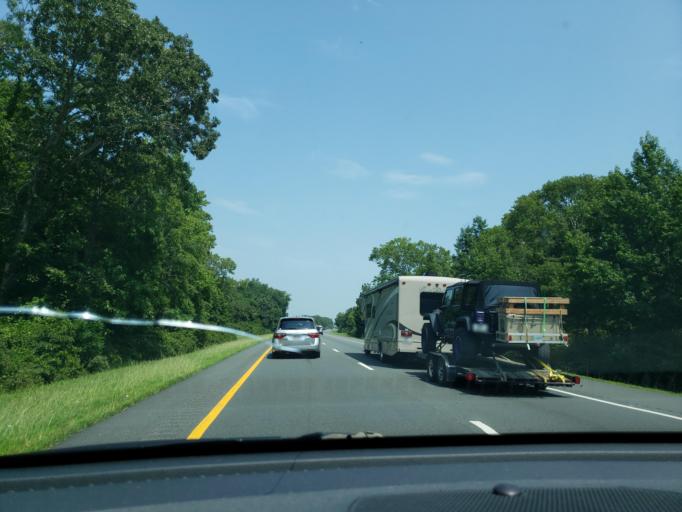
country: US
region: New Jersey
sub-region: Cape May County
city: Avalon
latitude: 39.1475
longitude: -74.7556
